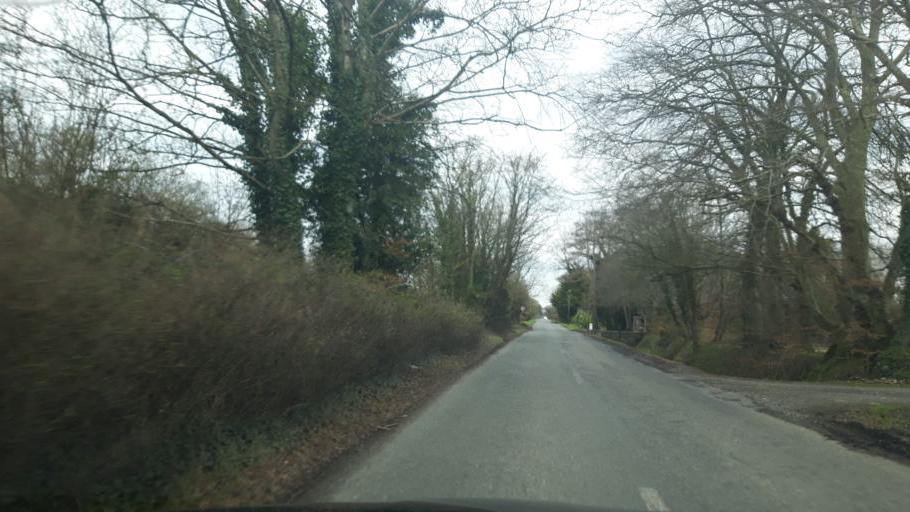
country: IE
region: Leinster
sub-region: Kildare
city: Clane
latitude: 53.3270
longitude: -6.6914
